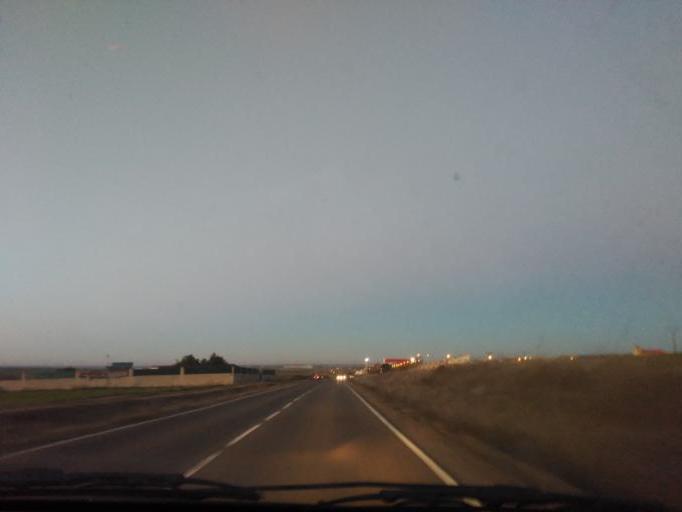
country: ES
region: Castille and Leon
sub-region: Provincia de Salamanca
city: Villares de la Reina
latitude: 41.0048
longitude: -5.6556
